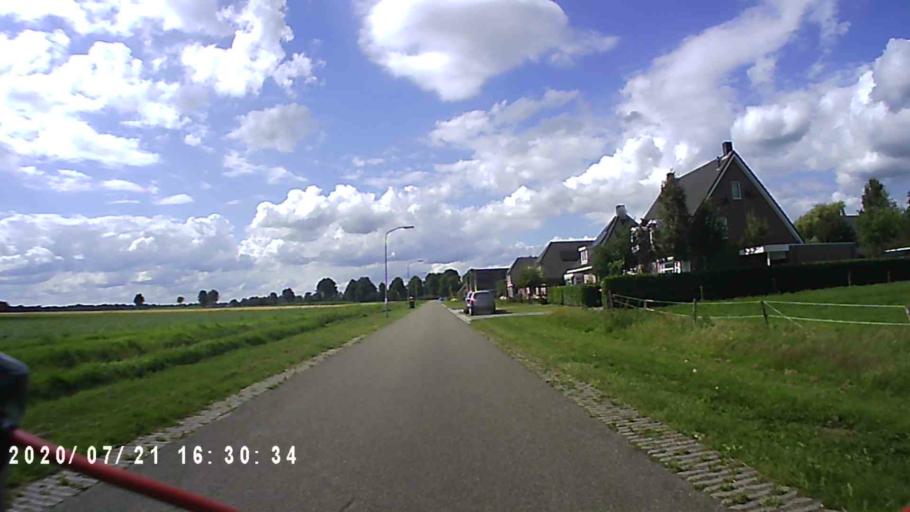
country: NL
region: Groningen
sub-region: Gemeente Hoogezand-Sappemeer
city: Sappemeer
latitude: 53.0827
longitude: 6.7921
